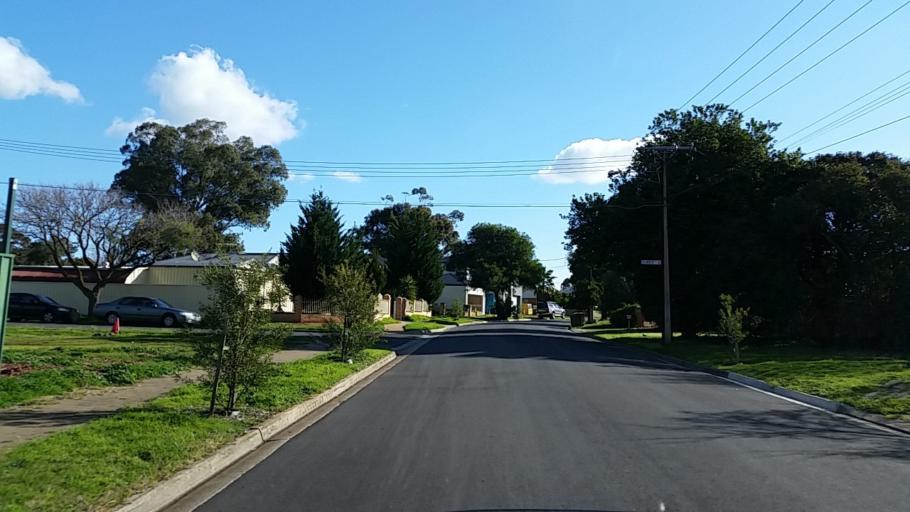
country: AU
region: South Australia
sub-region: Port Adelaide Enfield
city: Gilles Plains
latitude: -34.8546
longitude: 138.6682
